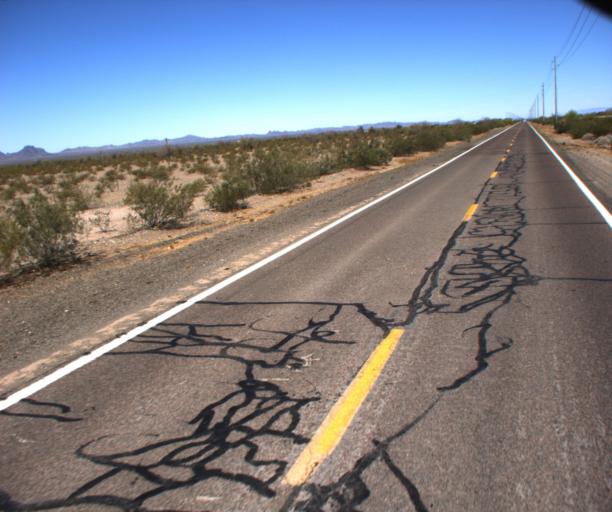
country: US
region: Arizona
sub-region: La Paz County
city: Salome
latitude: 33.7939
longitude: -113.8250
